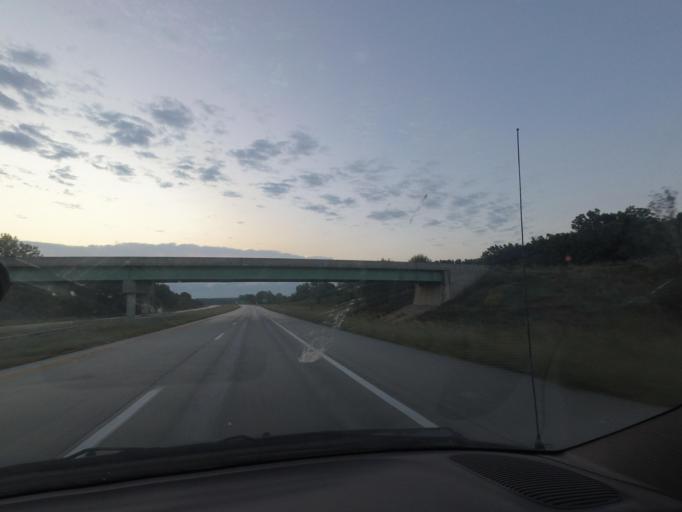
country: US
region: Missouri
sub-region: Macon County
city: Macon
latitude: 39.7516
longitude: -92.5309
